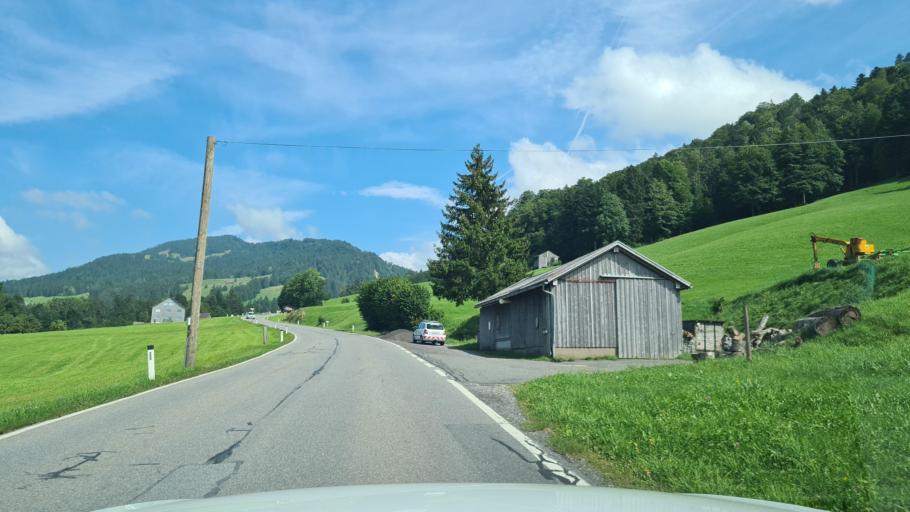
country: AT
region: Vorarlberg
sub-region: Politischer Bezirk Bregenz
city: Riefensberg
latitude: 47.4561
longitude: 9.9856
